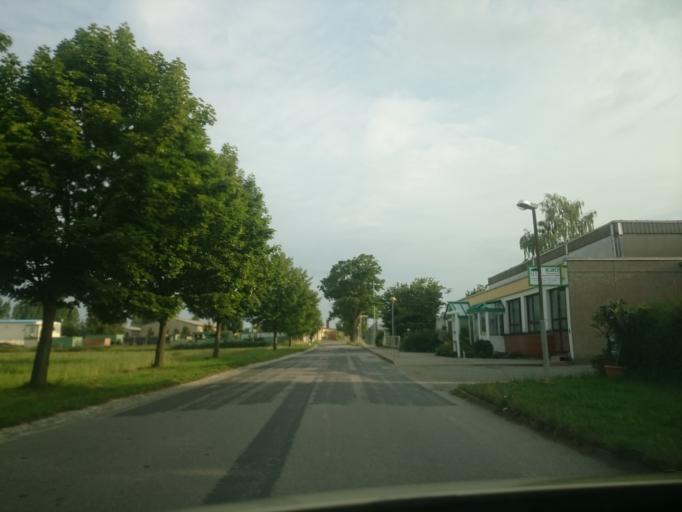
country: DE
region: Saxony
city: Leubsdorf
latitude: 50.7945
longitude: 13.1669
